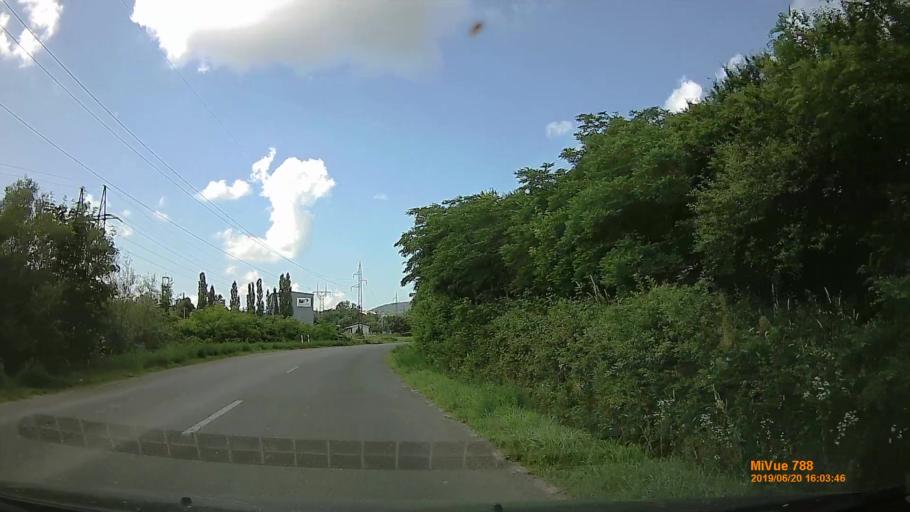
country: HU
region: Baranya
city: Pellerd
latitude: 46.0659
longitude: 18.1142
